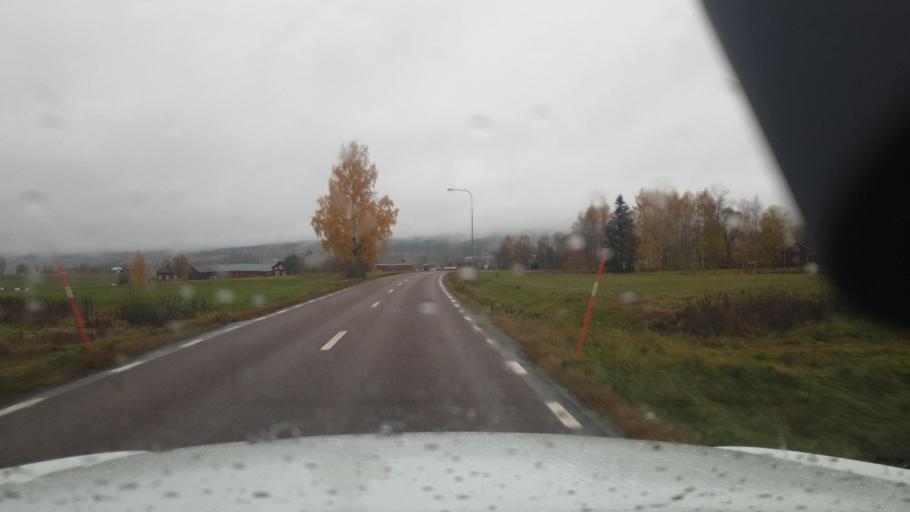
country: SE
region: Vaermland
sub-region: Sunne Kommun
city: Sunne
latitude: 59.8595
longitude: 12.9456
